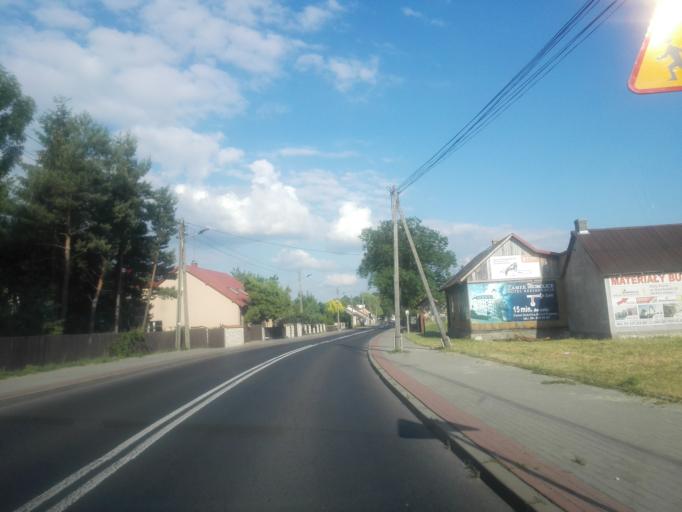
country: PL
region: Silesian Voivodeship
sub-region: Powiat czestochowski
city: Potok Zloty
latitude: 50.7235
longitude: 19.4303
